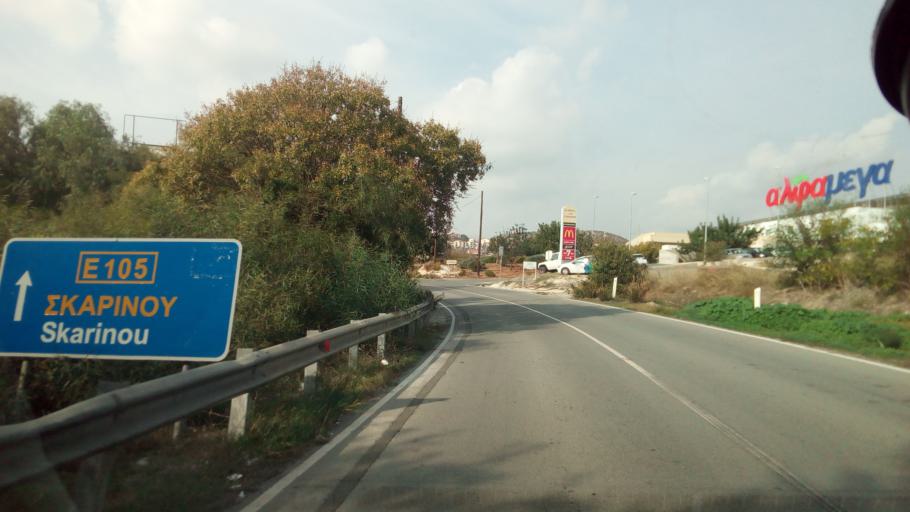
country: CY
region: Larnaka
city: Kofinou
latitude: 34.8165
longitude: 33.3606
